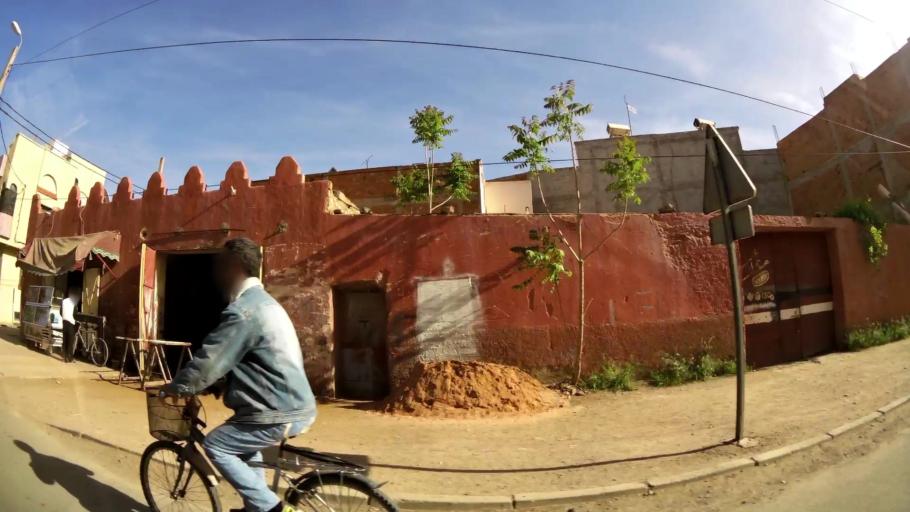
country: MA
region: Oriental
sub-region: Oujda-Angad
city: Oujda
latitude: 34.6749
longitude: -1.9084
